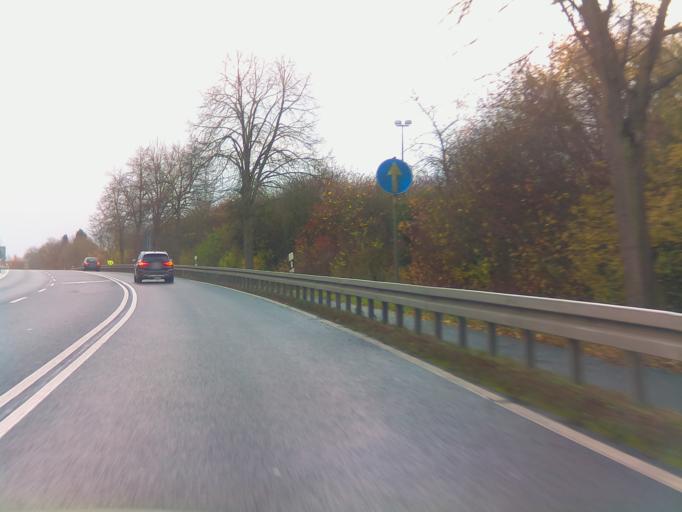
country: DE
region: Hesse
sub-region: Regierungsbezirk Kassel
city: Petersberg
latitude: 50.5519
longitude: 9.6992
